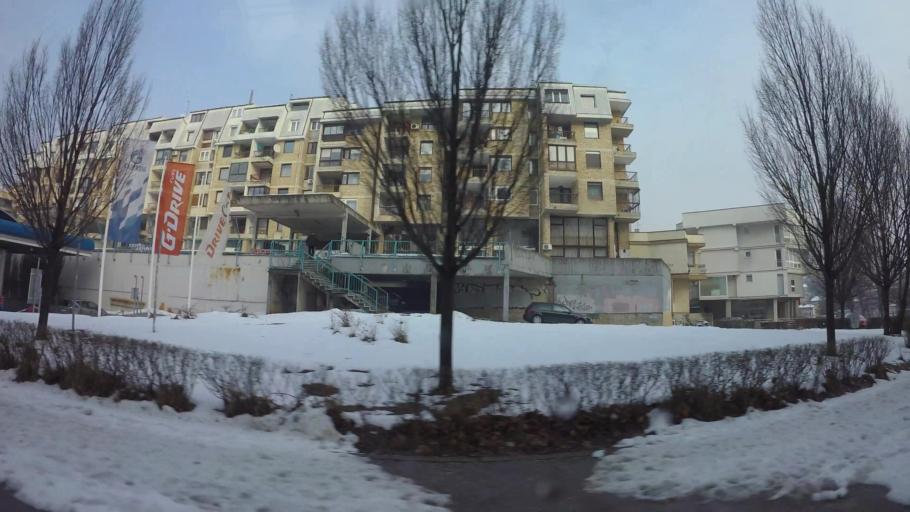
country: BA
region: Federation of Bosnia and Herzegovina
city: Kobilja Glava
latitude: 43.8699
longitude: 18.4161
